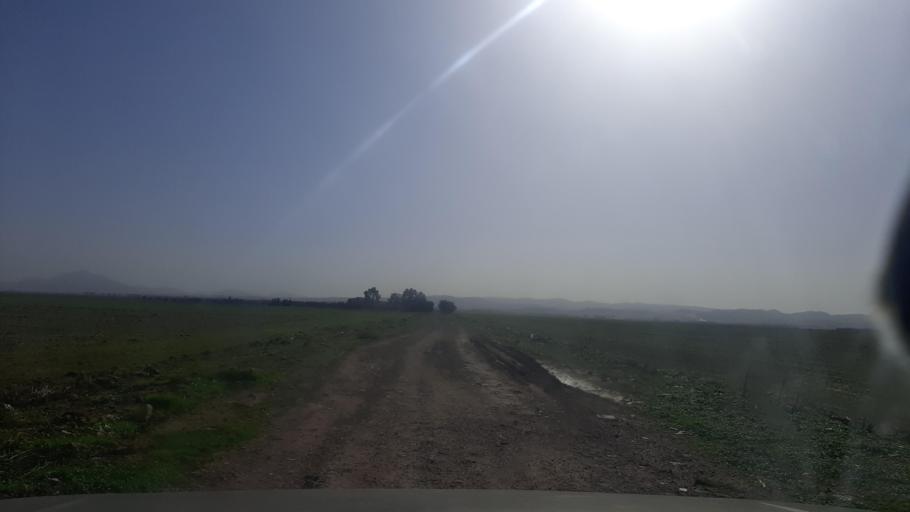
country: TN
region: Tunis
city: La Mohammedia
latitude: 36.6459
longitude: 10.0891
